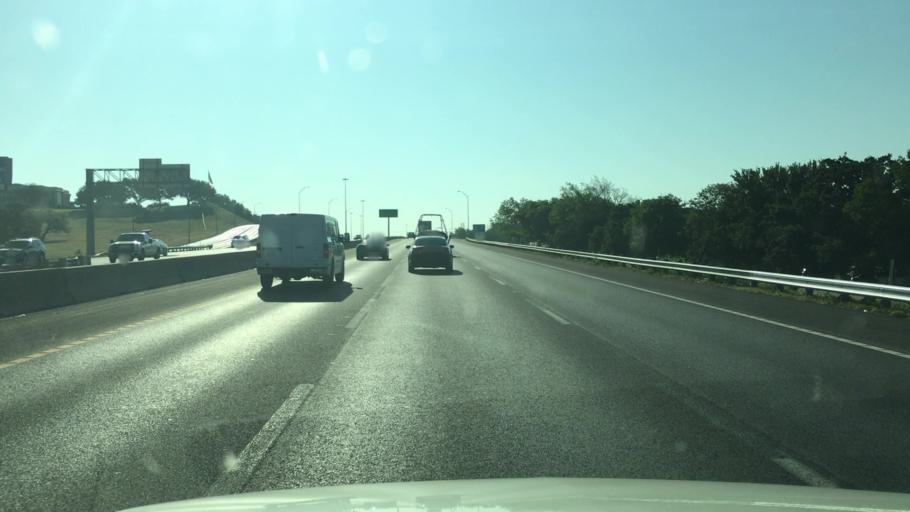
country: US
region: Texas
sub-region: Tarrant County
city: Haltom City
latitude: 32.7604
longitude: -97.2326
